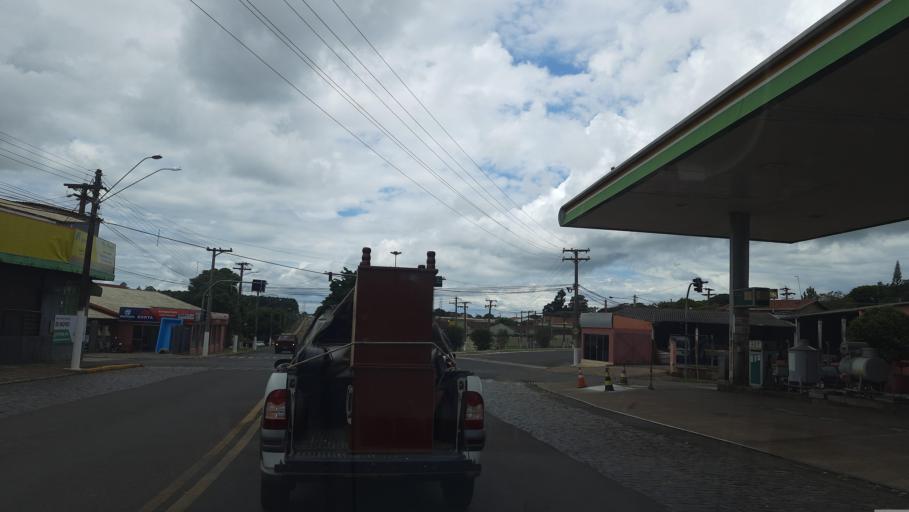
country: BR
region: Sao Paulo
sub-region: Casa Branca
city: Casa Branca
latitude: -21.7800
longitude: -47.0735
